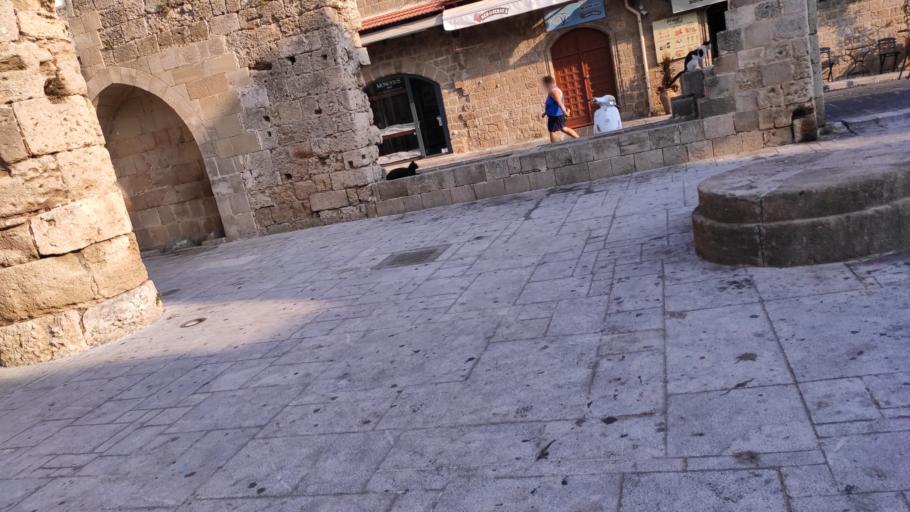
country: GR
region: South Aegean
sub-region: Nomos Dodekanisou
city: Rodos
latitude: 36.4428
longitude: 28.2307
